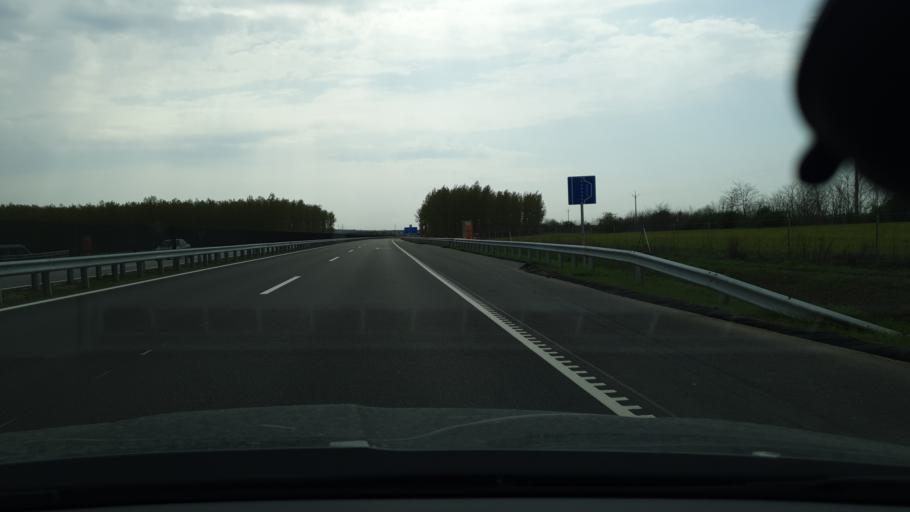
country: HU
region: Pest
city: Pilis
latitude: 47.3156
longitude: 19.5489
